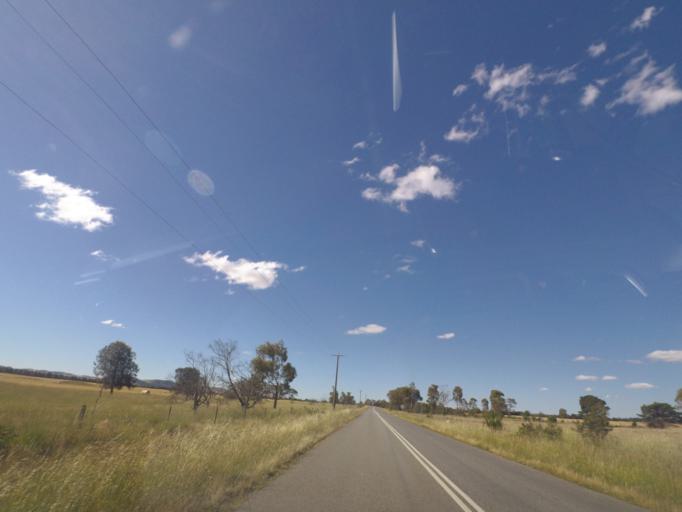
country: AU
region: Victoria
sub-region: Hume
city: Craigieburn
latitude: -37.4251
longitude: 144.8742
